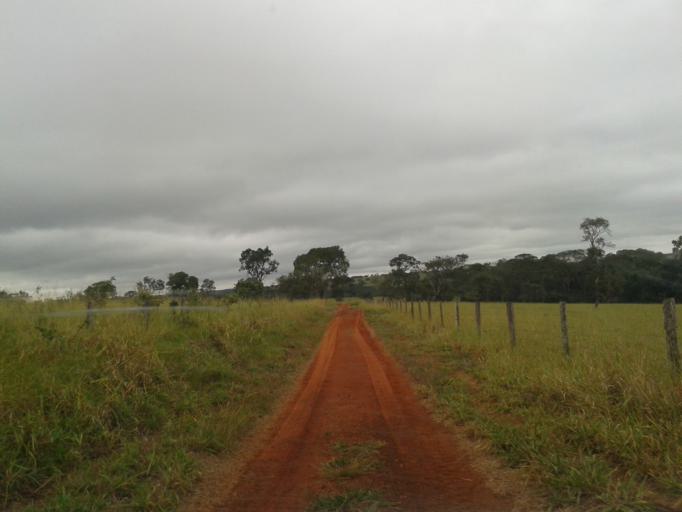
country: BR
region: Minas Gerais
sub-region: Campina Verde
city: Campina Verde
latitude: -19.4154
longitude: -49.6507
